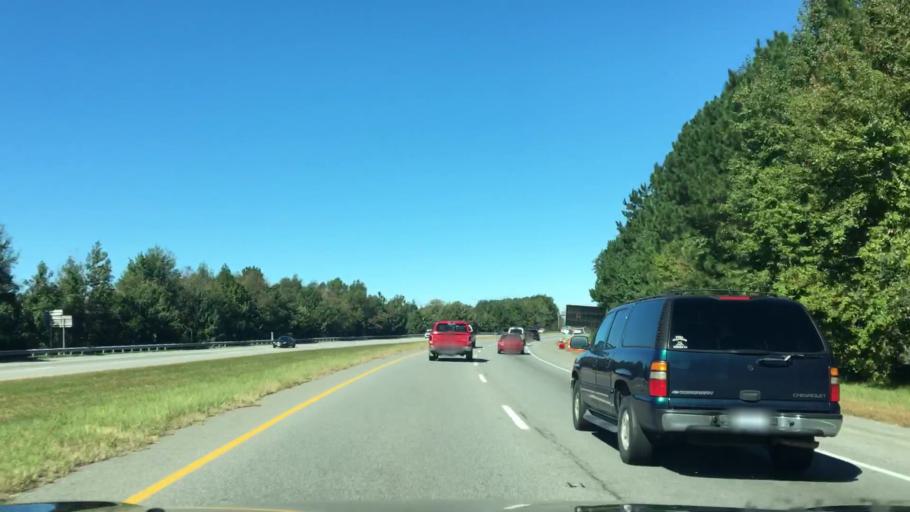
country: US
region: Virginia
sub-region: City of Chesapeake
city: Chesapeake
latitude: 36.7452
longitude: -76.2571
